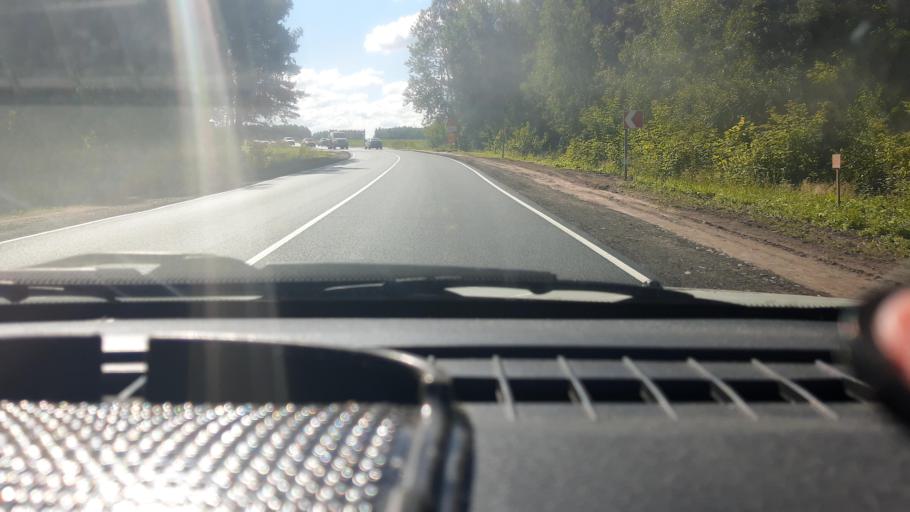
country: RU
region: Nizjnij Novgorod
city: Dal'neye Konstantinovo
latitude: 55.9585
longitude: 44.2099
